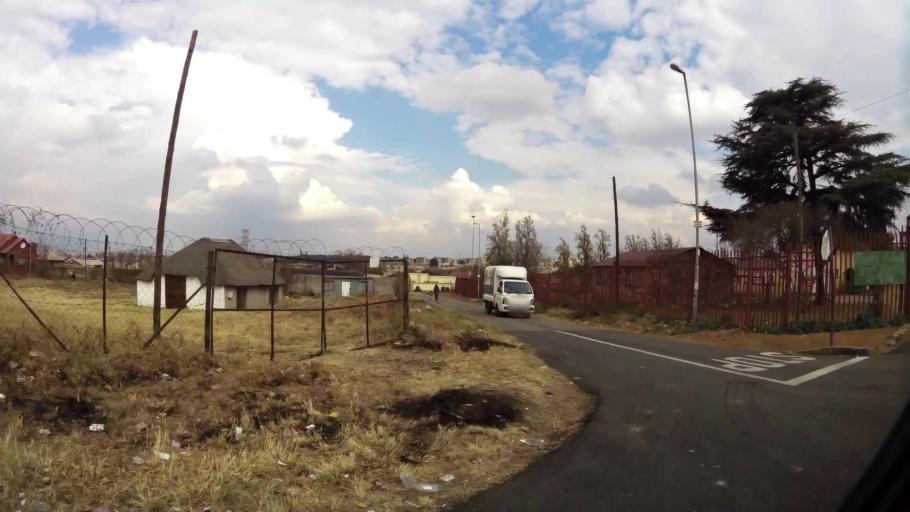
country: ZA
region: Gauteng
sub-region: City of Johannesburg Metropolitan Municipality
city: Soweto
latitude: -26.2354
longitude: 27.8661
